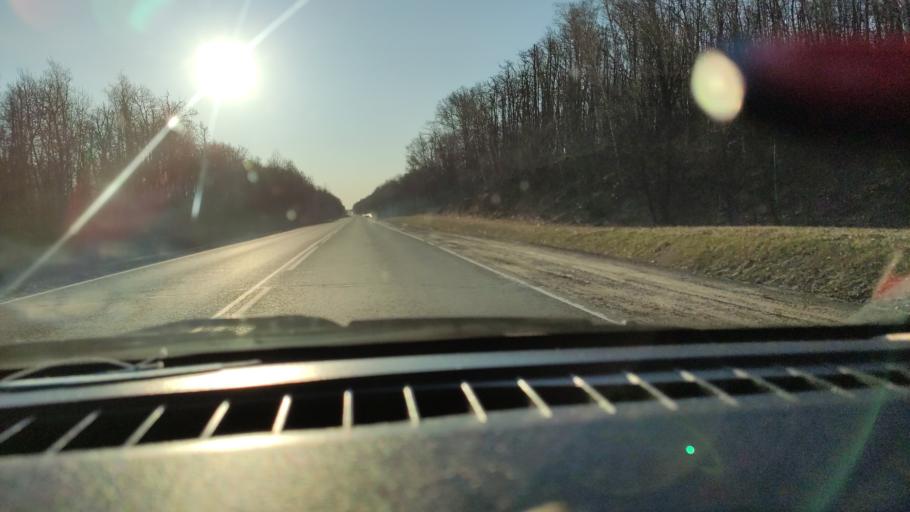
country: RU
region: Saratov
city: Vol'sk
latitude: 52.1116
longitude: 47.3288
